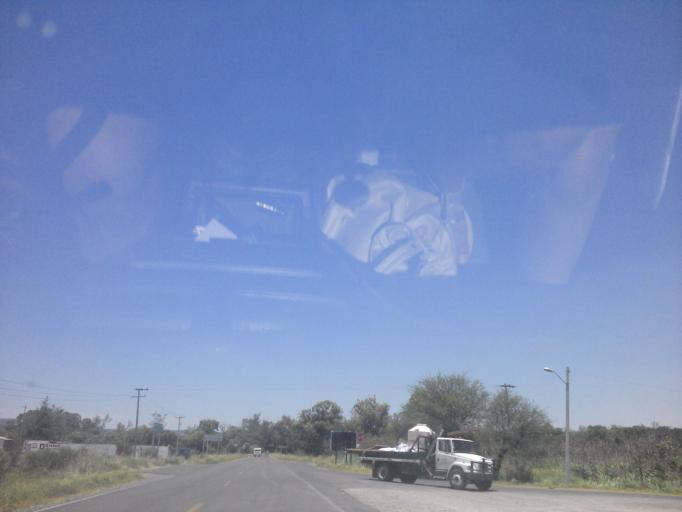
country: MX
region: Jalisco
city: San Diego de Alejandria
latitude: 20.8712
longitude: -101.9875
